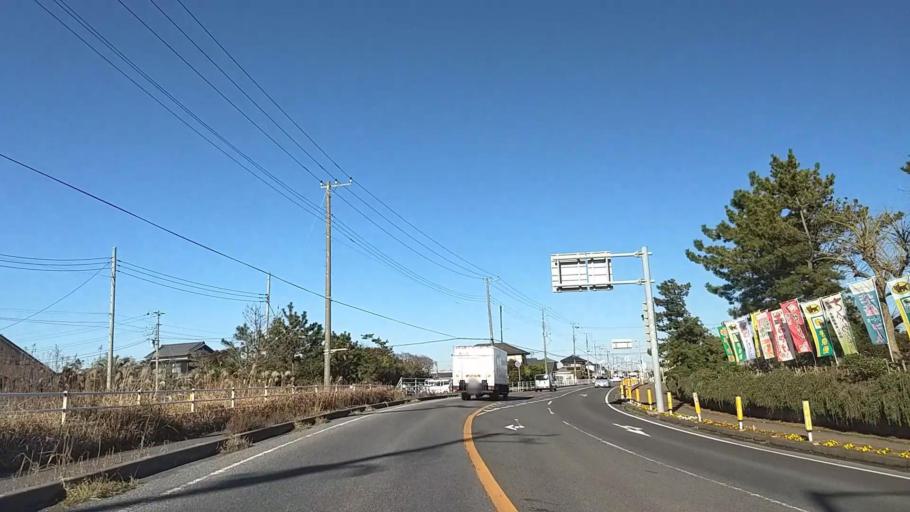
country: JP
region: Chiba
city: Togane
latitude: 35.5008
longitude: 140.4286
